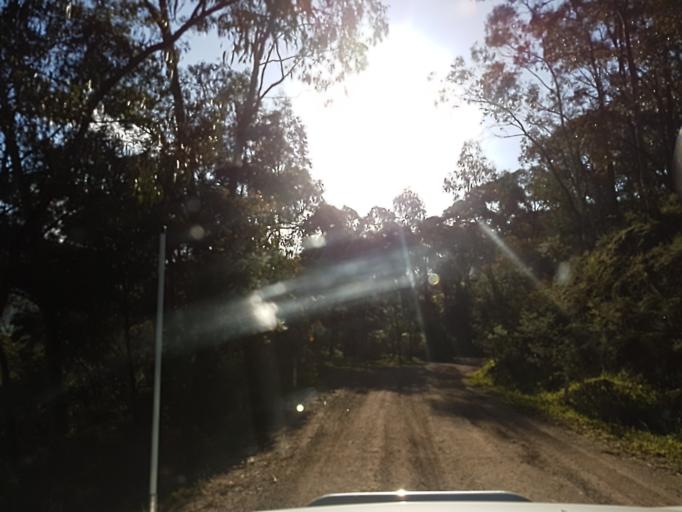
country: AU
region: Victoria
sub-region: East Gippsland
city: Bairnsdale
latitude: -37.4866
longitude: 147.1954
